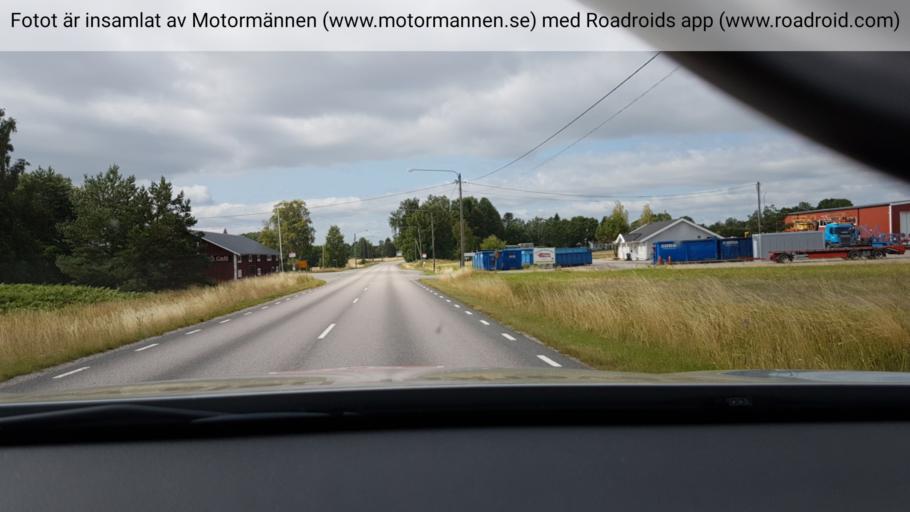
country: SE
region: Stockholm
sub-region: Norrtalje Kommun
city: Rimbo
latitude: 59.7016
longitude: 18.4060
